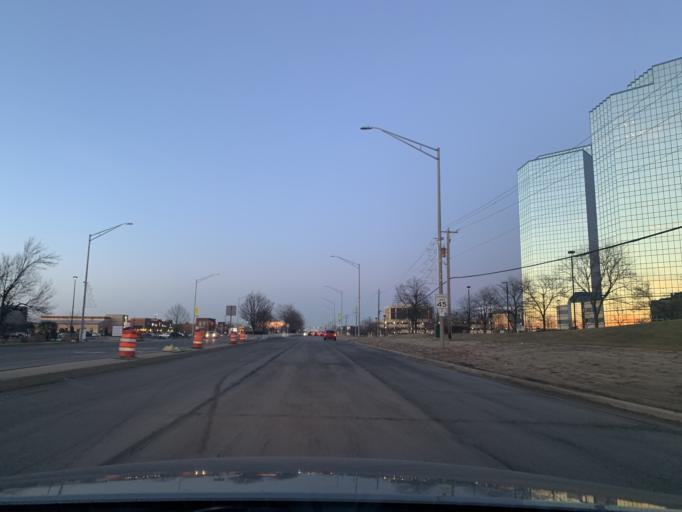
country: US
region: Illinois
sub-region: Cook County
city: Hoffman Estates
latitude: 42.0436
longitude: -88.0452
